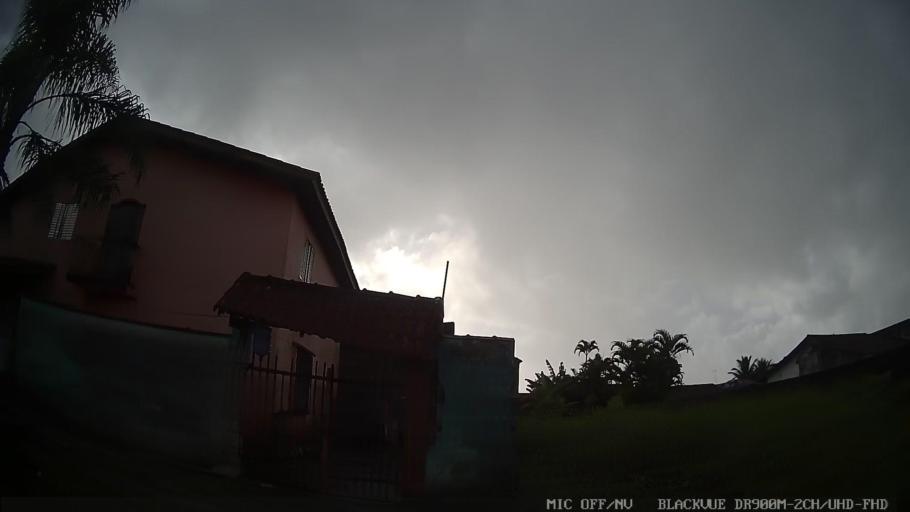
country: BR
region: Sao Paulo
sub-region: Itanhaem
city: Itanhaem
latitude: -24.2002
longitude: -46.8343
